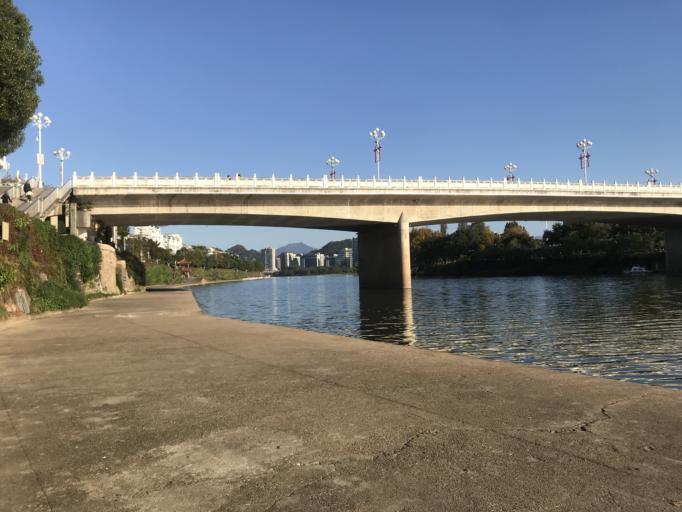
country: CN
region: Anhui Sheng
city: Huangshan
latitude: 29.7095
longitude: 118.3075
